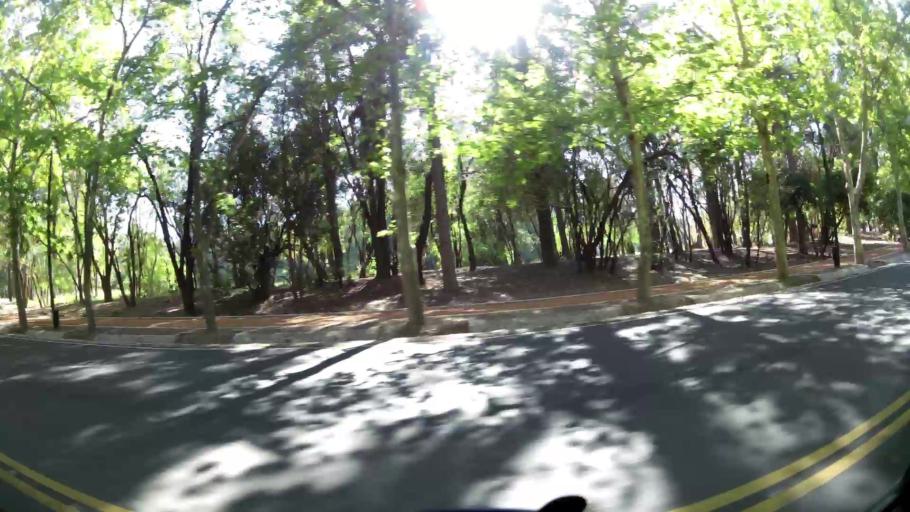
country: AR
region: Mendoza
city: Mendoza
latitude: -32.8874
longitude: -68.8727
